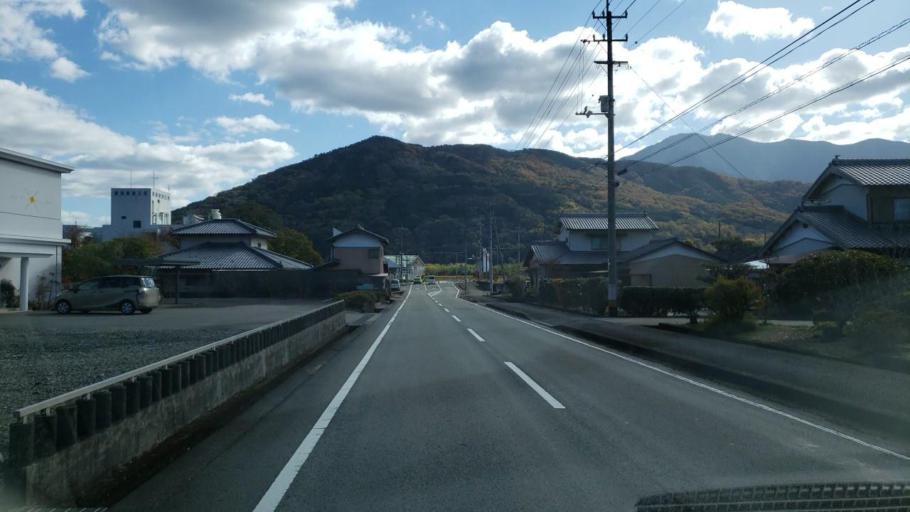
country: JP
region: Tokushima
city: Wakimachi
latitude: 34.0686
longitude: 134.1812
